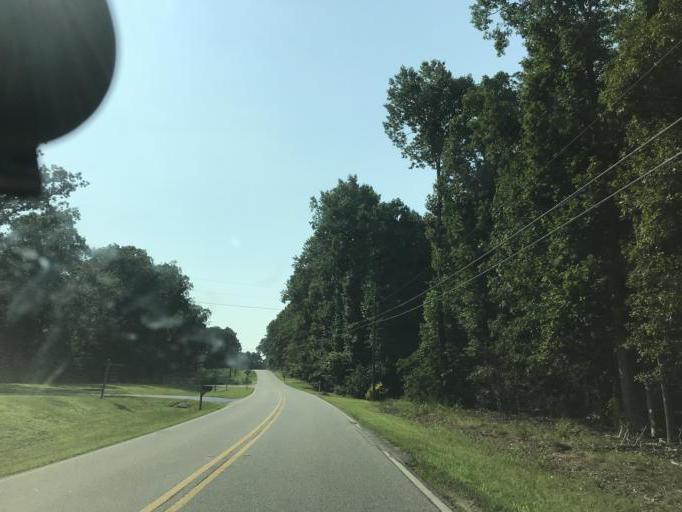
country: US
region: Georgia
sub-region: Forsyth County
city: Cumming
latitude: 34.2377
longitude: -84.1085
